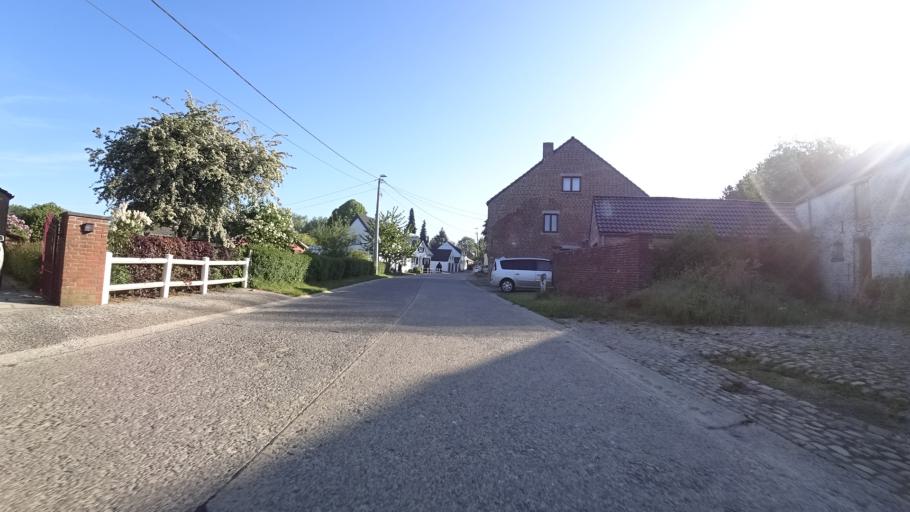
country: BE
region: Wallonia
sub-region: Province du Brabant Wallon
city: Walhain-Saint-Paul
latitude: 50.6352
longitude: 4.6734
